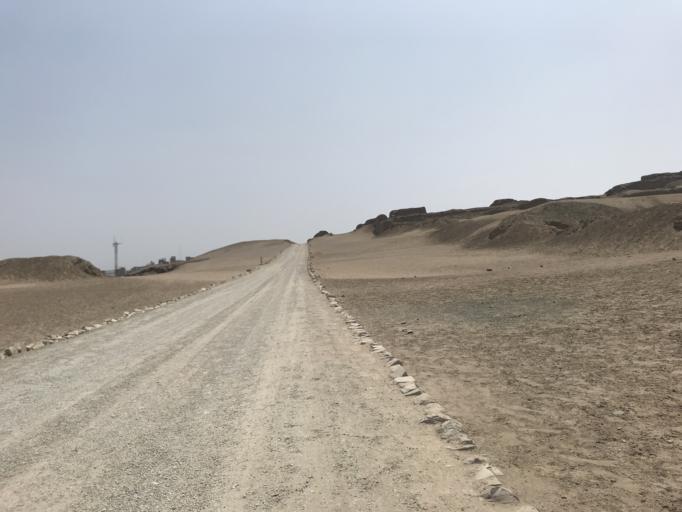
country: PE
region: Lima
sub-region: Lima
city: Punta Hermosa
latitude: -12.2553
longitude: -76.9002
